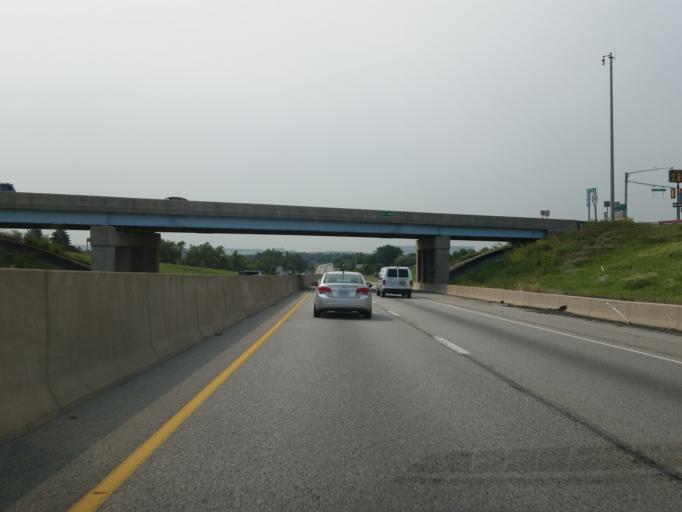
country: US
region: Pennsylvania
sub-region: York County
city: Manchester
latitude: 40.0827
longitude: -76.7656
